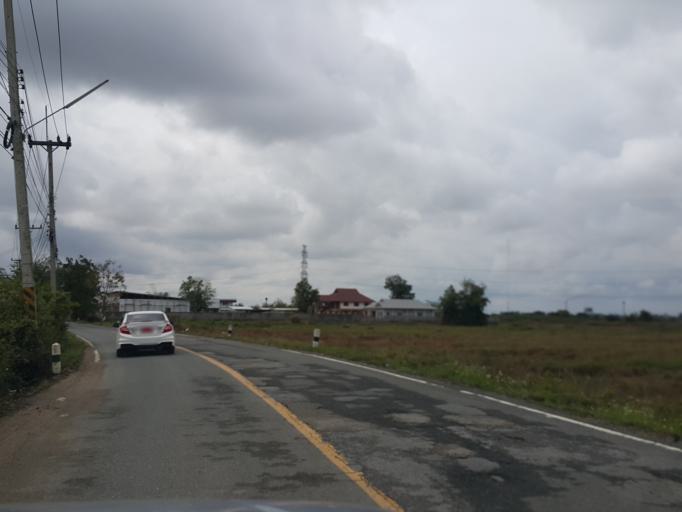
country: TH
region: Lamphun
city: Lamphun
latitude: 18.5571
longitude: 99.0589
